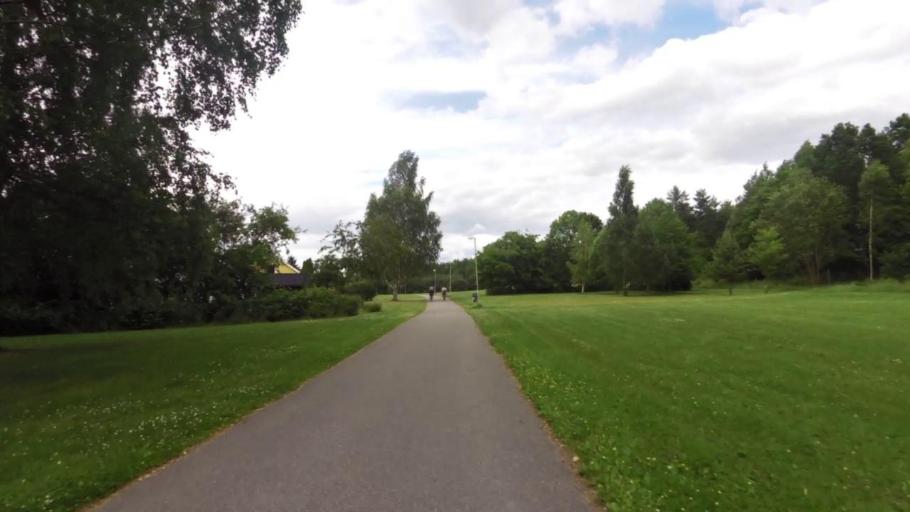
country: SE
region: OEstergoetland
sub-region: Linkopings Kommun
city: Malmslatt
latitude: 58.4174
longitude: 15.5662
